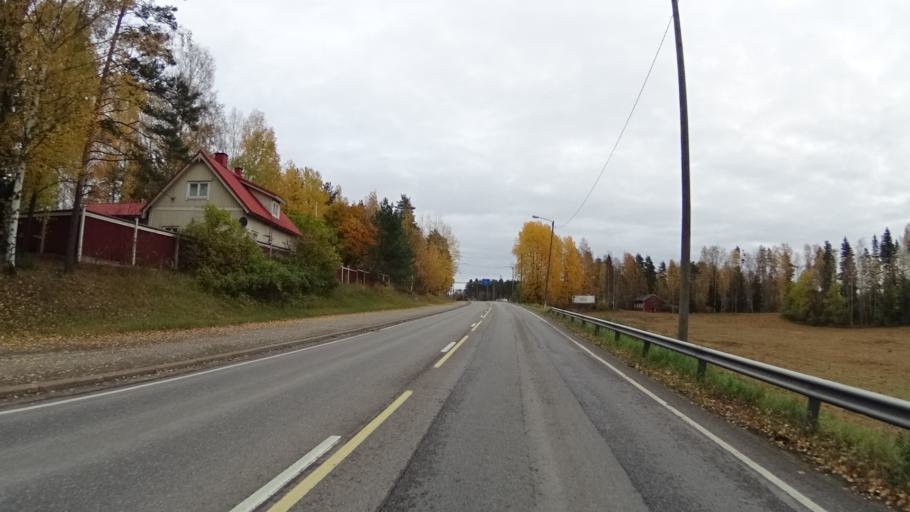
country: FI
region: South Karelia
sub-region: Lappeenranta
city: Lemi
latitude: 60.9592
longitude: 27.7979
